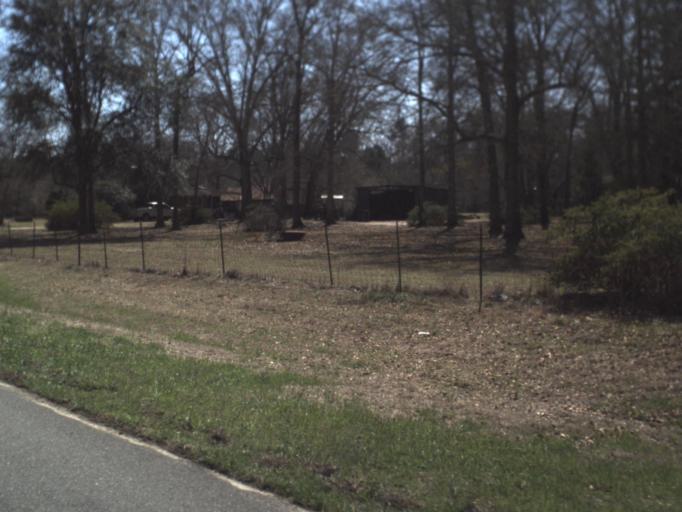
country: US
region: Florida
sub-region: Jackson County
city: Sneads
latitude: 30.6314
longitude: -85.0311
